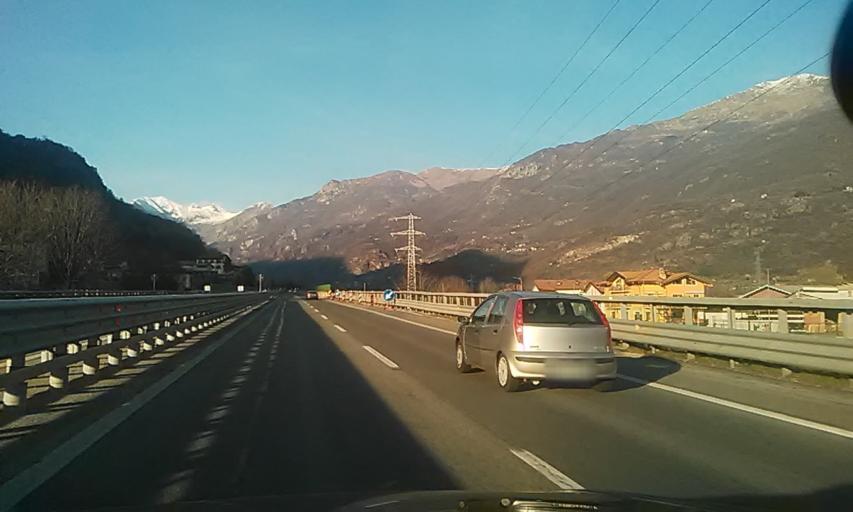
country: IT
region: Piedmont
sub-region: Provincia di Torino
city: Quassolo
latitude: 45.5222
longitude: 7.8346
